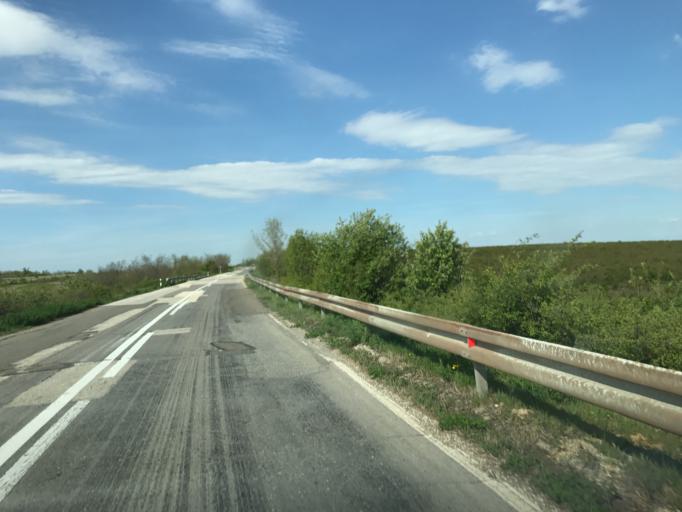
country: RS
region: Central Serbia
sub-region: Zajecarski Okrug
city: Zajecar
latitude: 44.0023
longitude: 22.3016
